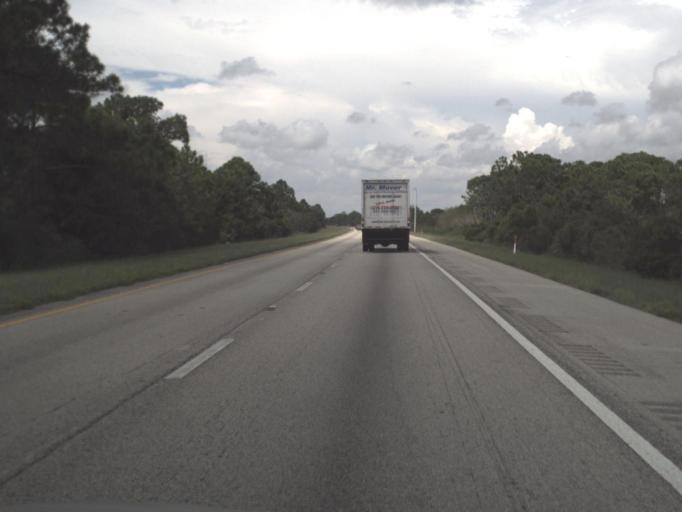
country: US
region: Florida
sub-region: Lee County
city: Suncoast Estates
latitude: 26.7950
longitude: -81.9086
